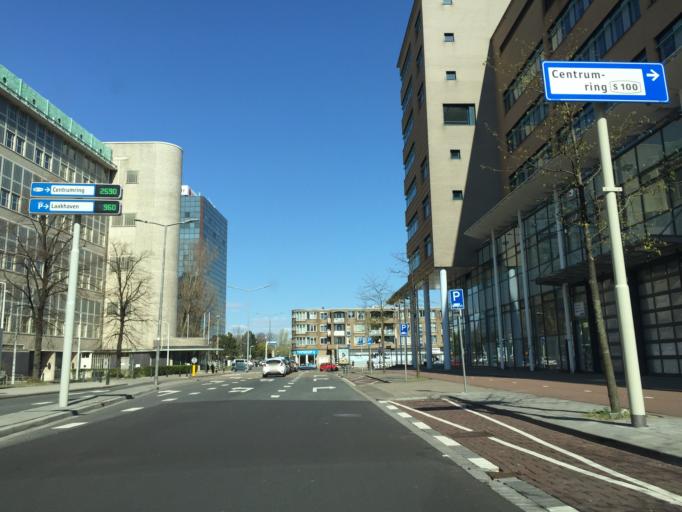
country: NL
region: South Holland
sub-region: Gemeente Den Haag
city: The Hague
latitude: 52.0695
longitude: 4.3248
